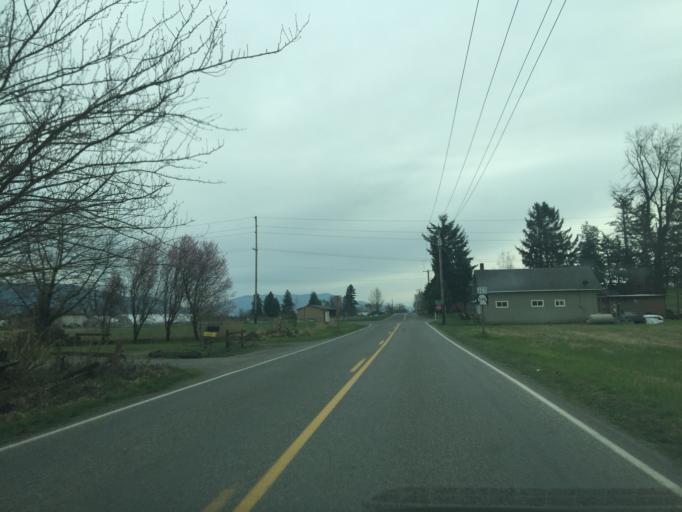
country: US
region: Washington
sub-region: Whatcom County
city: Nooksack
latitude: 48.9649
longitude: -122.3312
